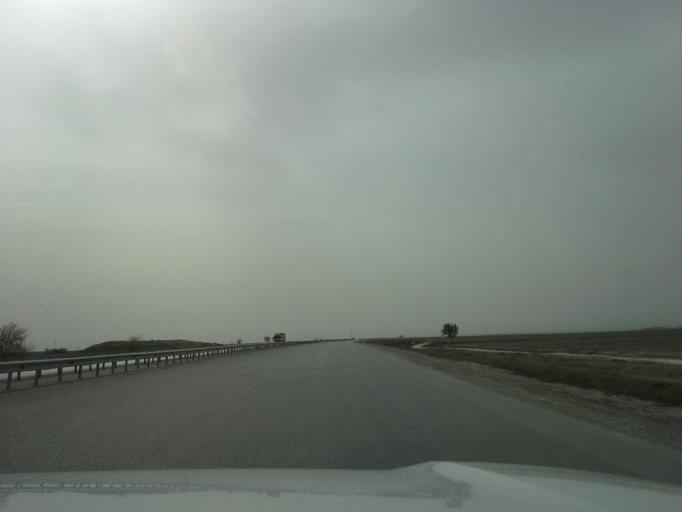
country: TM
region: Ahal
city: Kaka
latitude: 37.4701
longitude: 59.4995
